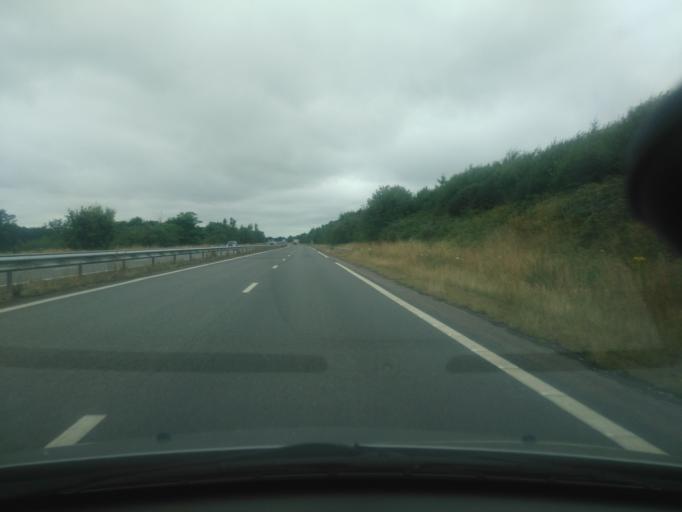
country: FR
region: Brittany
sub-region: Departement des Cotes-d'Armor
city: Plelan-le-Petit
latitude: 48.4203
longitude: -2.2702
